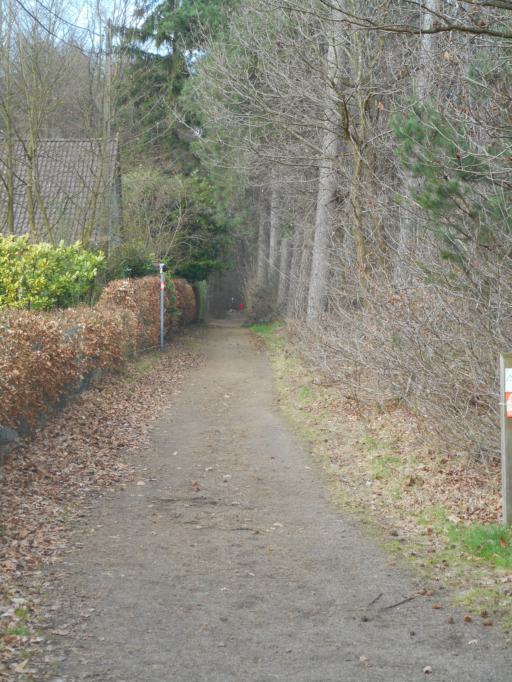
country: BE
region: Flanders
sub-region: Provincie Antwerpen
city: Westerlo
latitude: 51.0523
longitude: 4.9210
